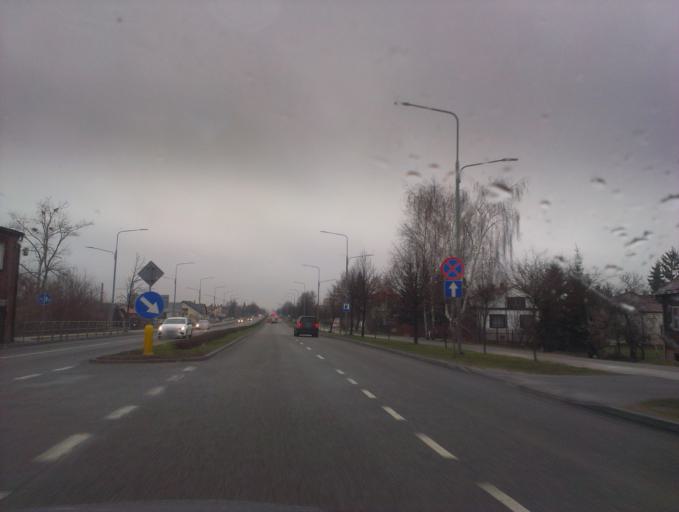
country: PL
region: Masovian Voivodeship
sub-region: Radom
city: Radom
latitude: 51.4195
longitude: 21.1525
